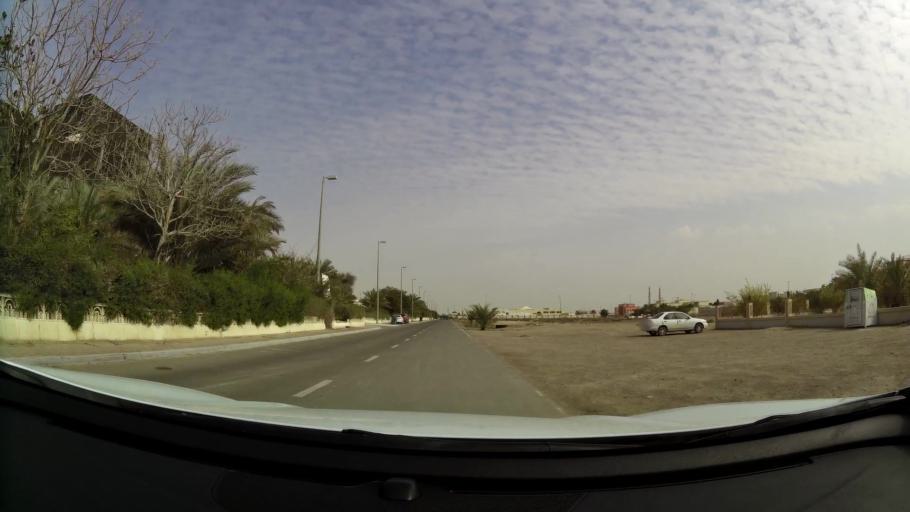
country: AE
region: Abu Dhabi
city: Abu Dhabi
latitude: 24.5980
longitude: 54.6961
